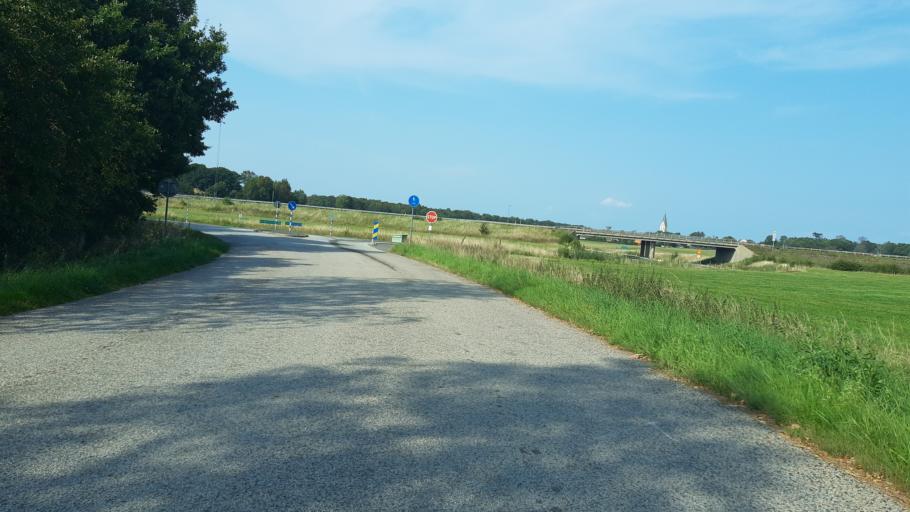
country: SE
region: Blekinge
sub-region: Ronneby Kommun
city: Brakne-Hoby
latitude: 56.2169
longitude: 15.1201
